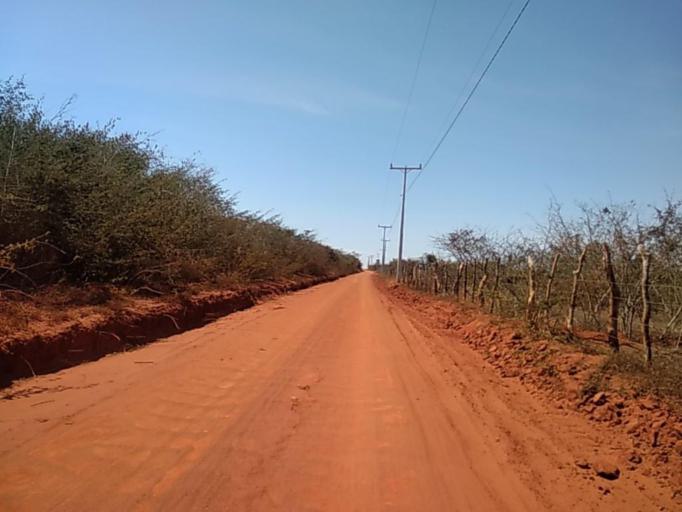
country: BR
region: Bahia
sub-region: Caetite
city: Caetite
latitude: -13.9853
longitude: -42.5098
